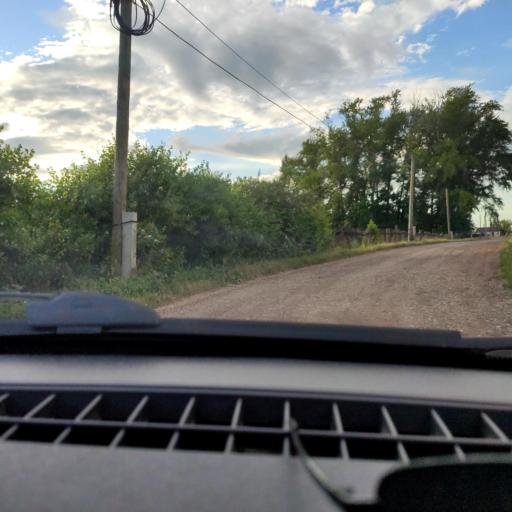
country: RU
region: Bashkortostan
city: Chishmy
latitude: 54.3744
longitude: 55.4206
